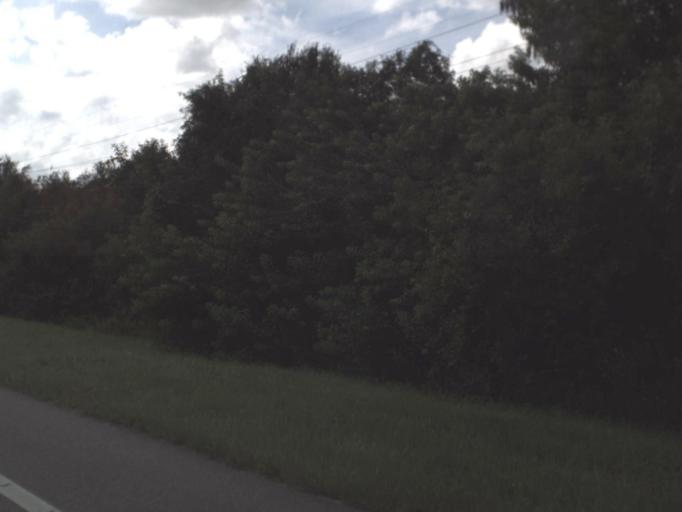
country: US
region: Florida
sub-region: Collier County
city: Immokalee
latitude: 26.3538
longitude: -81.3437
